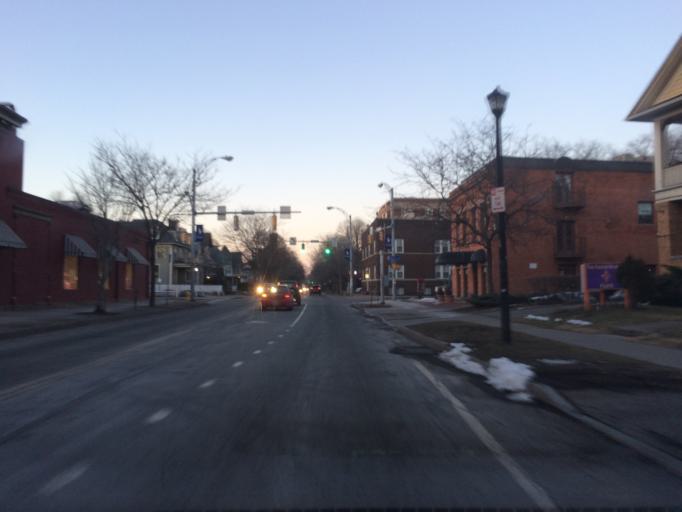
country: US
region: New York
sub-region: Monroe County
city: Rochester
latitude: 43.1499
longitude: -77.5902
